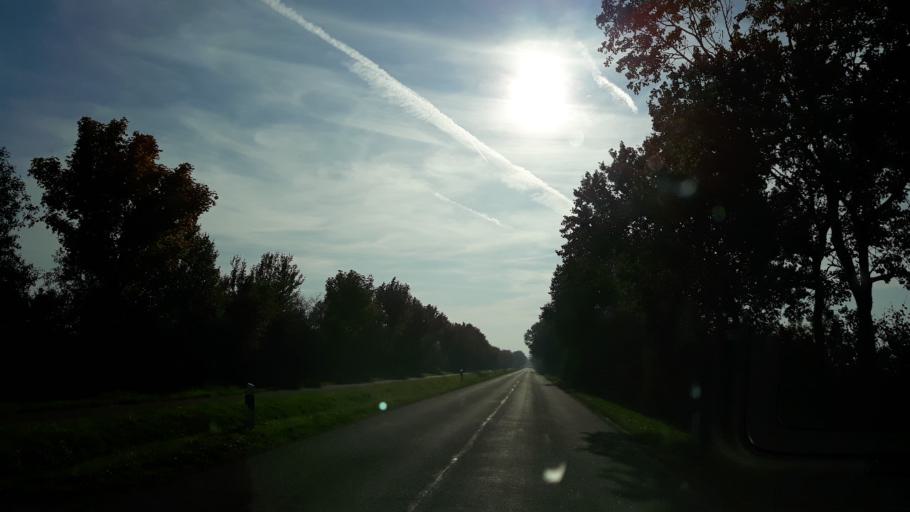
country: DE
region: Schleswig-Holstein
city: Gross Rheide
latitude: 54.4267
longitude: 9.4089
